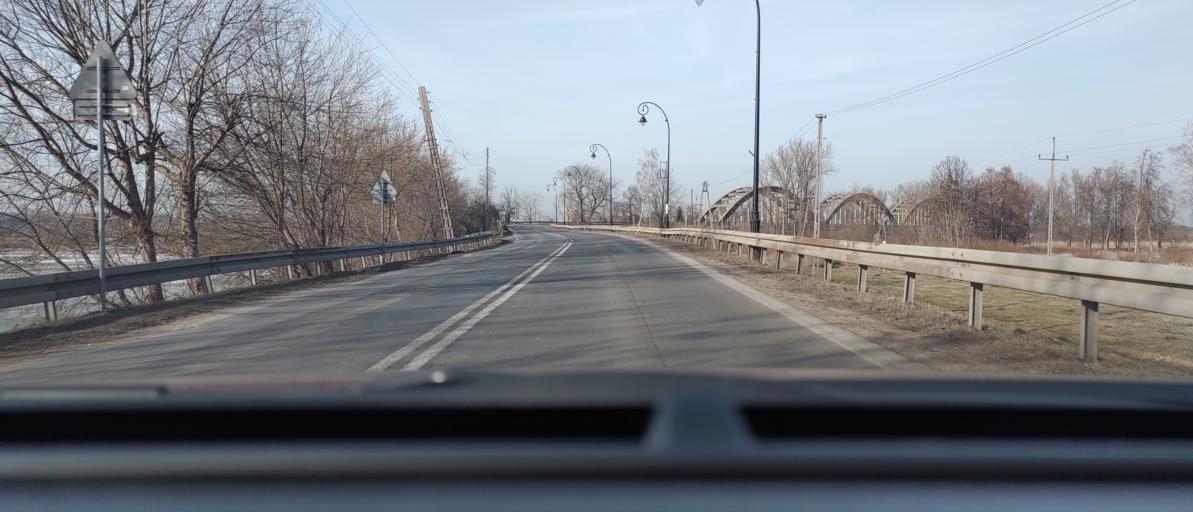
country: PL
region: Masovian Voivodeship
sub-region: Powiat bialobrzeski
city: Bialobrzegi
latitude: 51.6547
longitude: 20.9514
